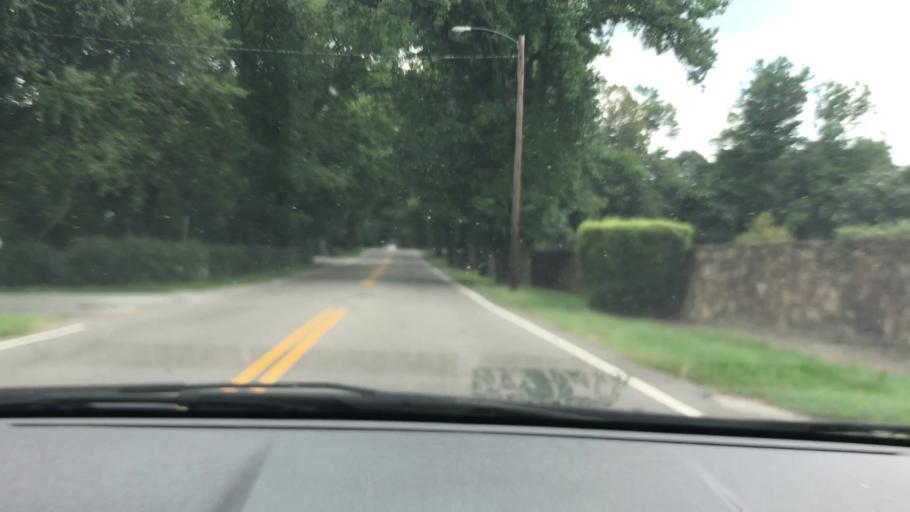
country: US
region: Virginia
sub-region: Henrico County
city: Dumbarton
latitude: 37.5649
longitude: -77.5074
